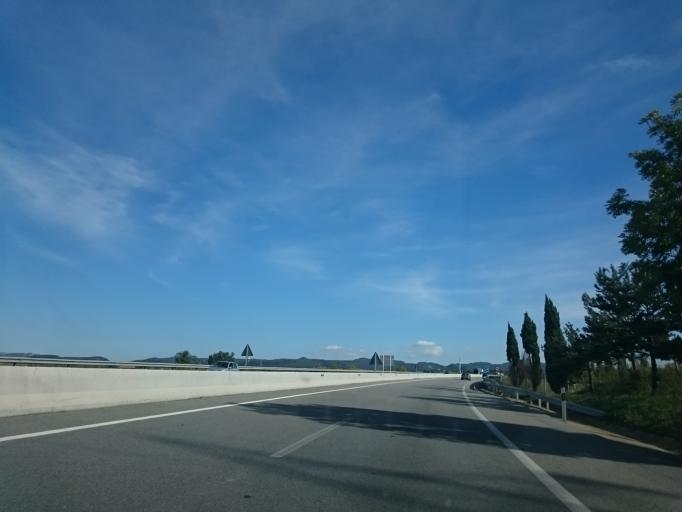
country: ES
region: Catalonia
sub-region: Provincia de Barcelona
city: Vic
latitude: 41.9592
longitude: 2.2819
